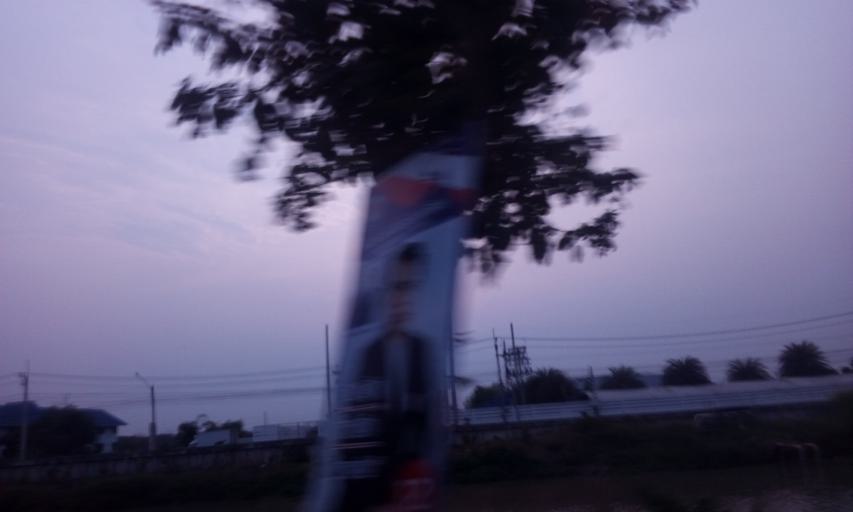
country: TH
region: Pathum Thani
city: Ban Lam Luk Ka
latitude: 13.9938
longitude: 100.8951
